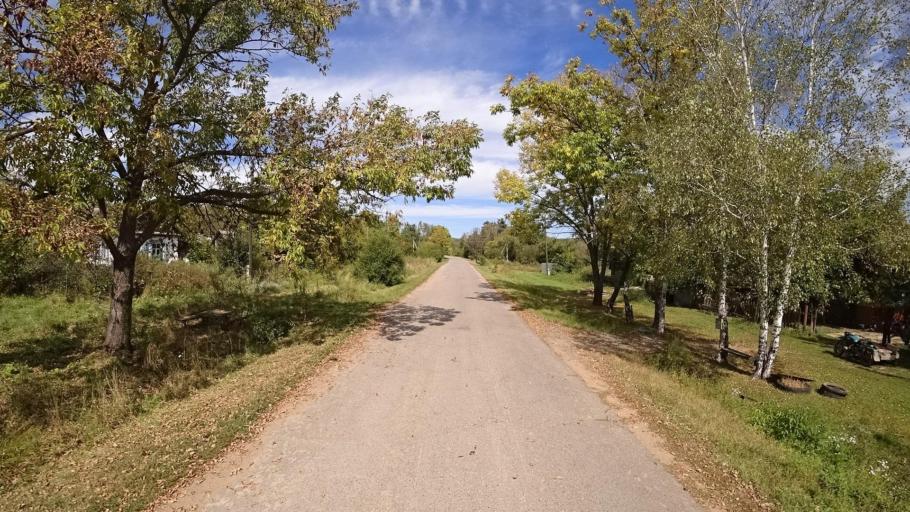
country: RU
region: Primorskiy
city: Yakovlevka
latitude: 44.6483
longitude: 133.5971
